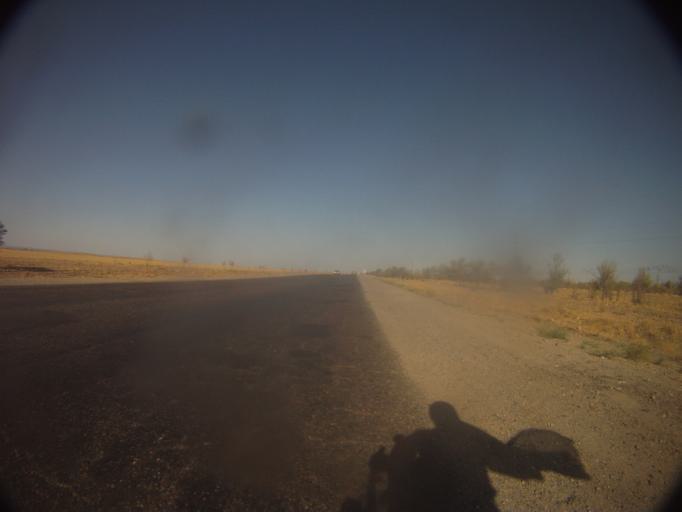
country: KZ
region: Zhambyl
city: Sarykemer
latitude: 42.9756
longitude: 71.5699
